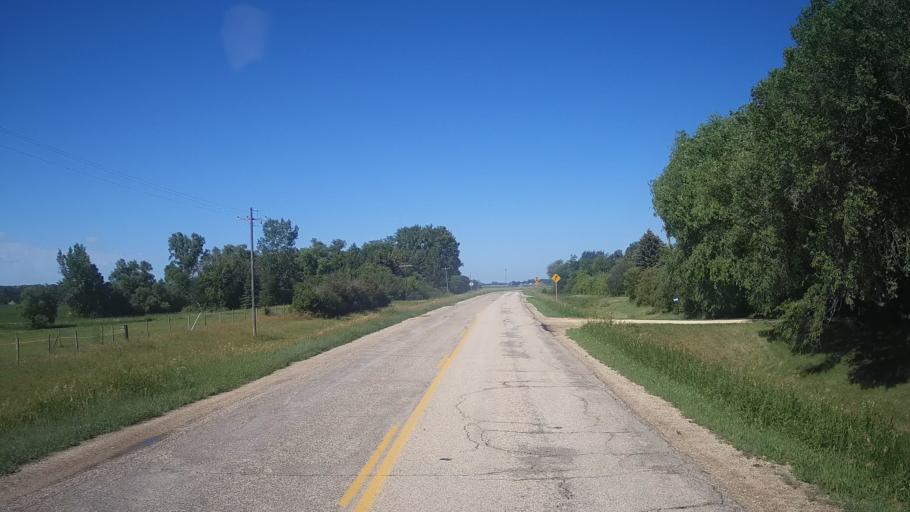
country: CA
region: Manitoba
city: Portage la Prairie
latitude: 50.0446
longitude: -98.0282
